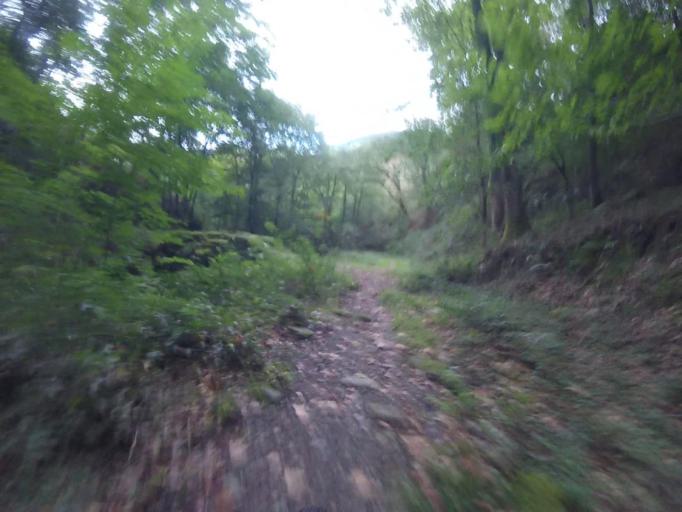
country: ES
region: Basque Country
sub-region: Provincia de Guipuzcoa
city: Errenteria
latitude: 43.2710
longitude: -1.8398
